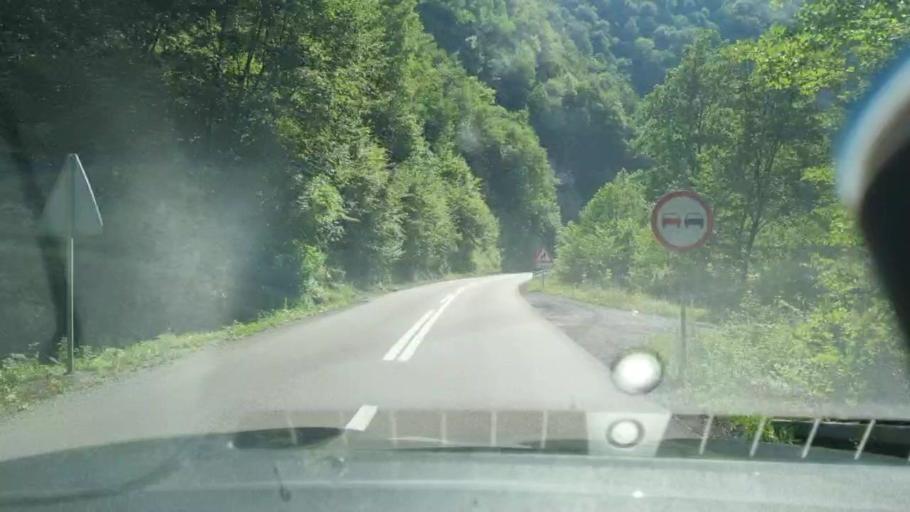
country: BA
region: Federation of Bosnia and Herzegovina
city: Bosanska Krupa
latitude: 44.8657
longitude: 16.0946
